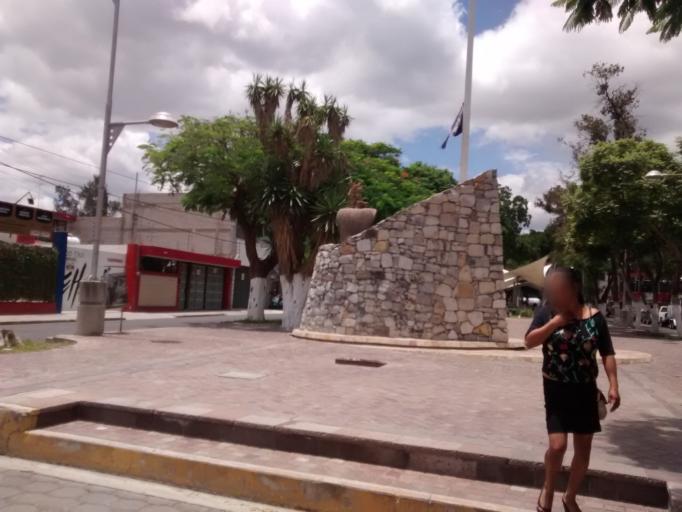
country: MX
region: Puebla
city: Tehuacan
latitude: 18.4525
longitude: -97.3927
